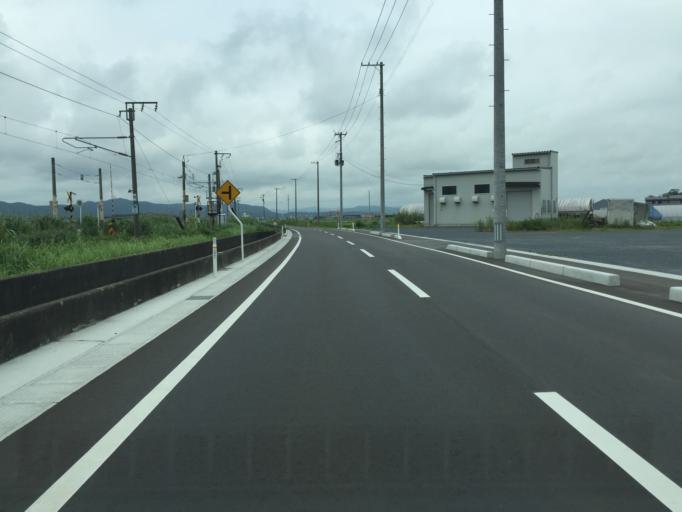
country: JP
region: Miyagi
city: Watari
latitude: 38.0224
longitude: 140.8804
